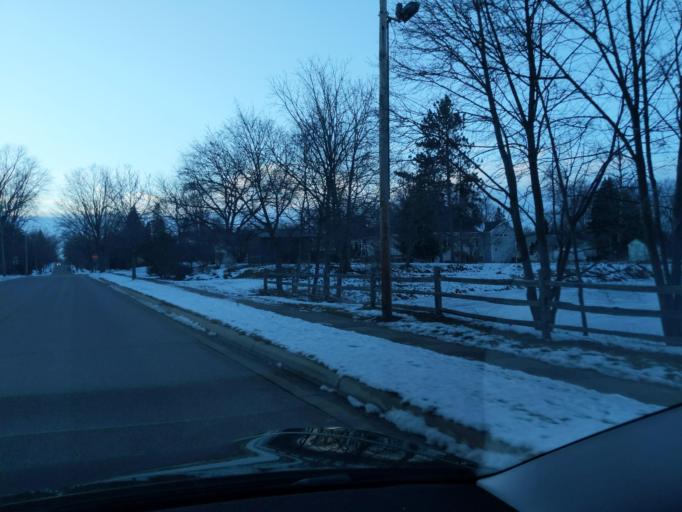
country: US
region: Michigan
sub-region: Ingham County
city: Mason
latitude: 42.5802
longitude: -84.4347
